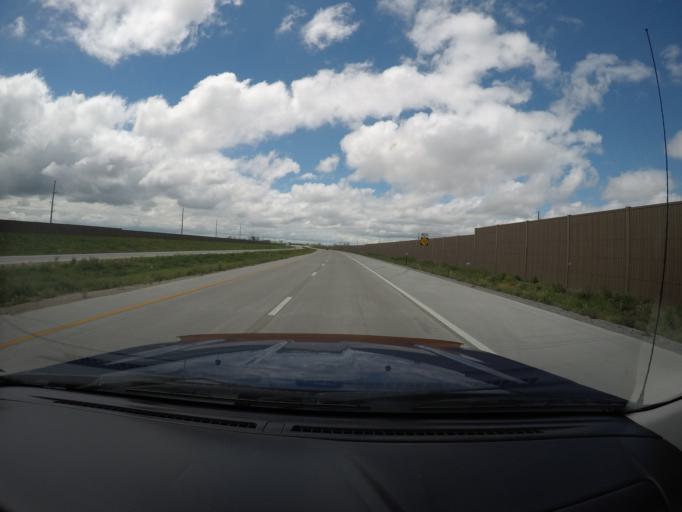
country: US
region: Kansas
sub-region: Douglas County
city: Lawrence
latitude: 38.9260
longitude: -95.2275
